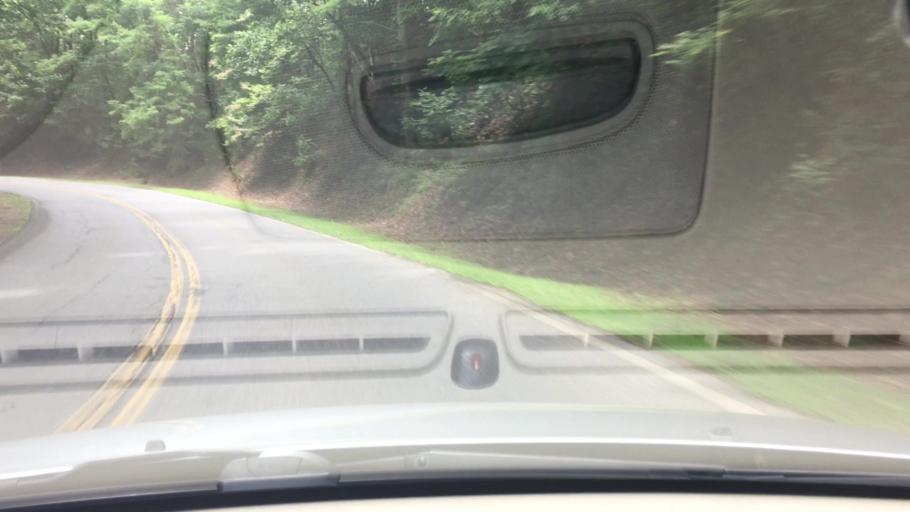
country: US
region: Georgia
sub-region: Dawson County
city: Dawsonville
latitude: 34.5647
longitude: -84.2530
